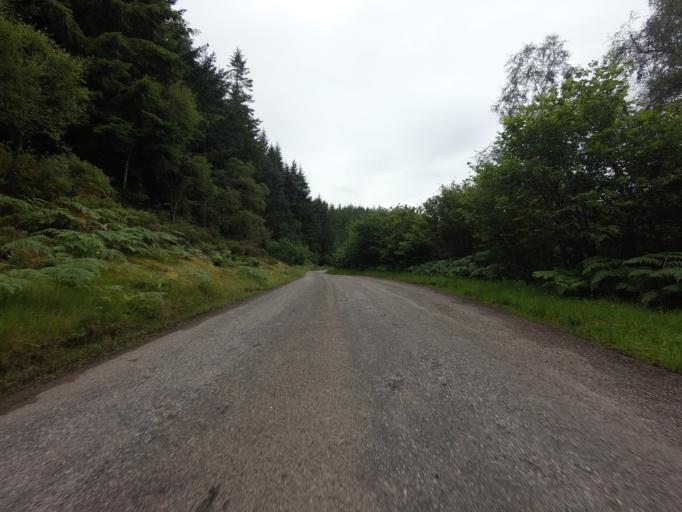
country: GB
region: Scotland
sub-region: Highland
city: Evanton
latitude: 57.9640
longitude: -4.4098
